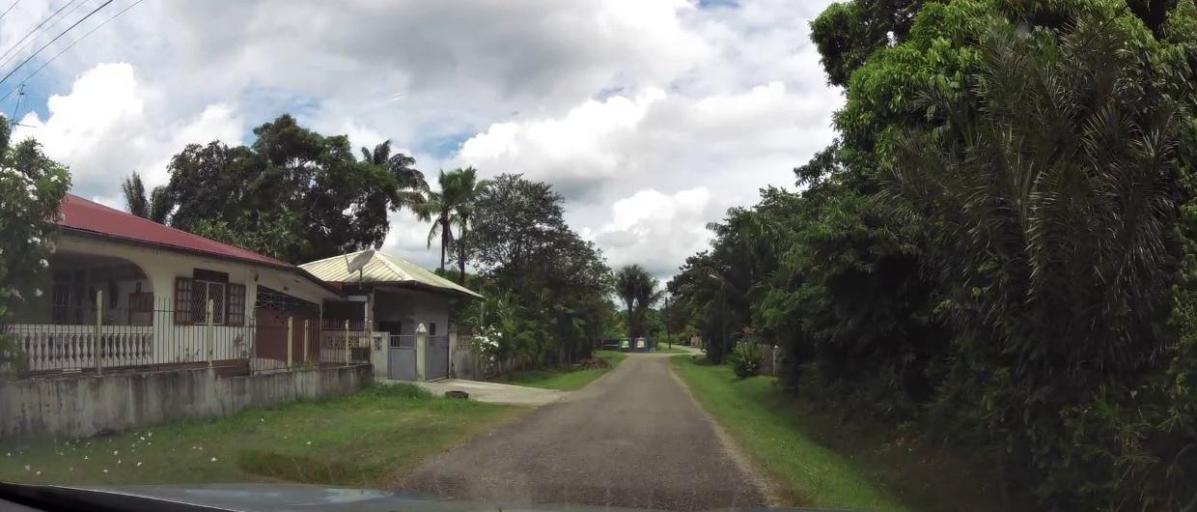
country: GF
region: Guyane
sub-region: Guyane
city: Sinnamary
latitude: 5.3735
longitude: -52.9575
